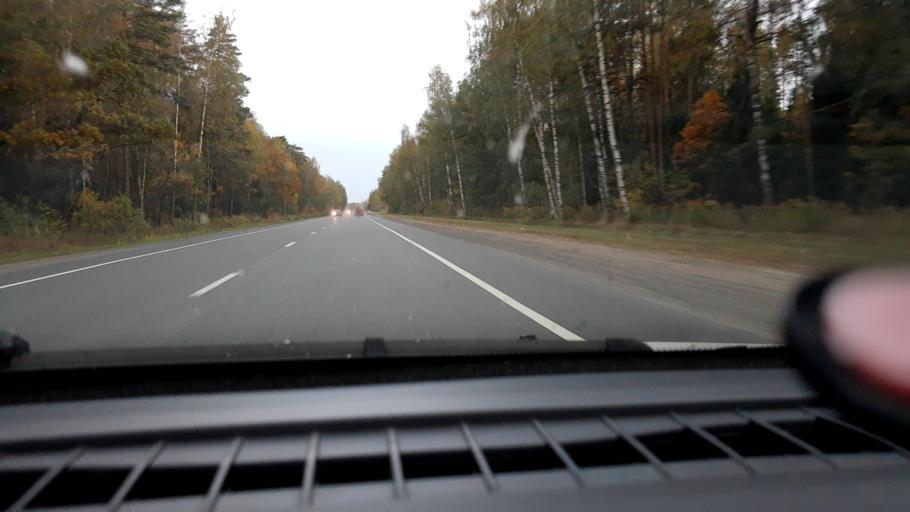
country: RU
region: Vladimir
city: Orgtrud
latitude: 56.2066
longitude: 40.7008
